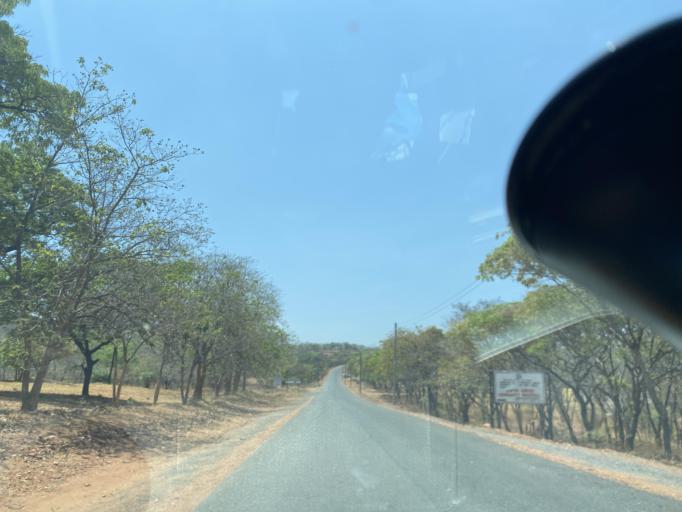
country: ZM
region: Lusaka
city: Kafue
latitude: -15.8663
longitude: 28.4461
